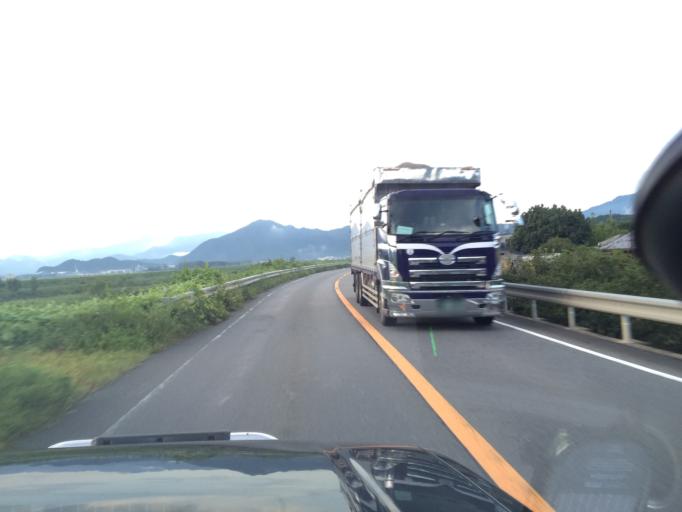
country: JP
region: Hyogo
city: Nishiwaki
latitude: 35.1427
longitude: 135.0293
